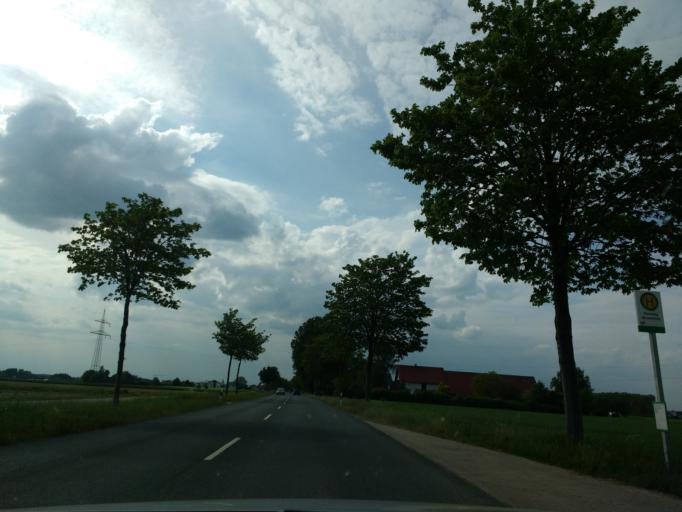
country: DE
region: North Rhine-Westphalia
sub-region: Regierungsbezirk Detmold
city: Salzkotten
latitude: 51.6654
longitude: 8.6390
